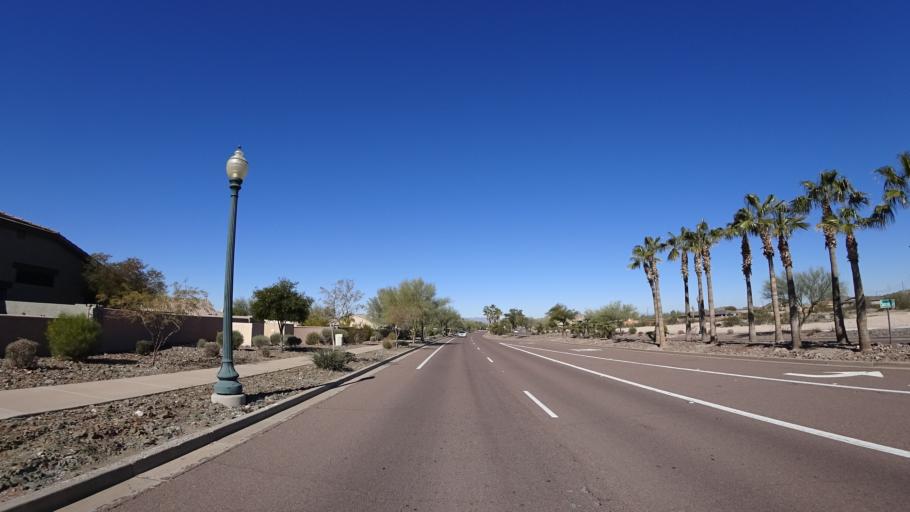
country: US
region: Arizona
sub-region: Maricopa County
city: Goodyear
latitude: 33.3468
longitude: -112.4274
